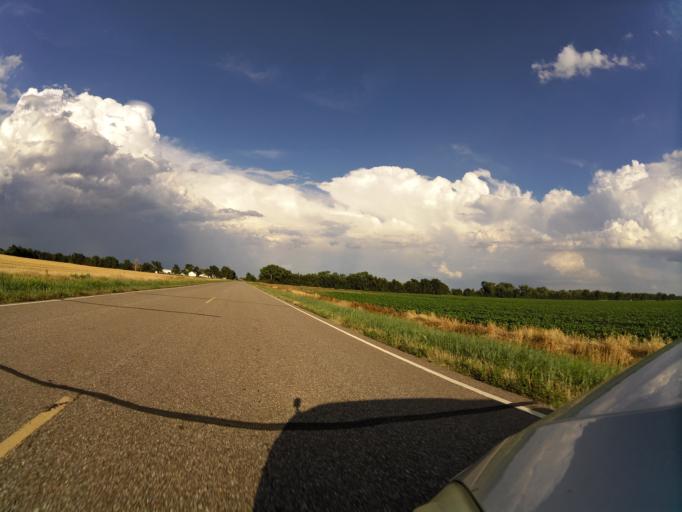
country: US
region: Kansas
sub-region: Reno County
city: South Hutchinson
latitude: 37.9410
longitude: -97.8982
